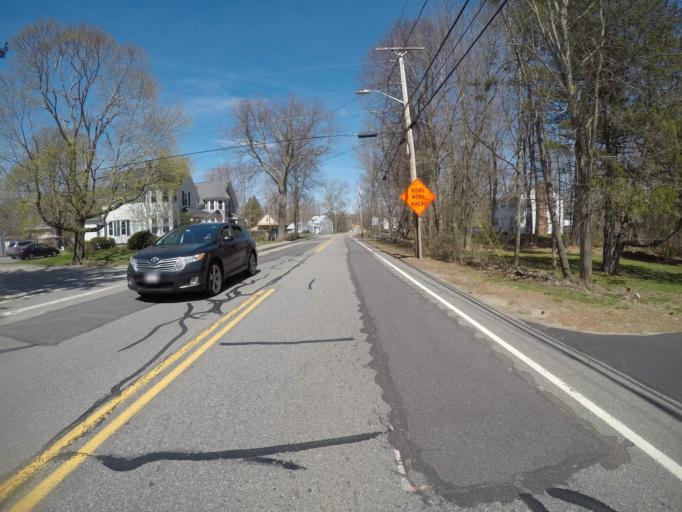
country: US
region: Massachusetts
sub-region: Bristol County
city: Easton
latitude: 42.0455
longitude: -71.0839
